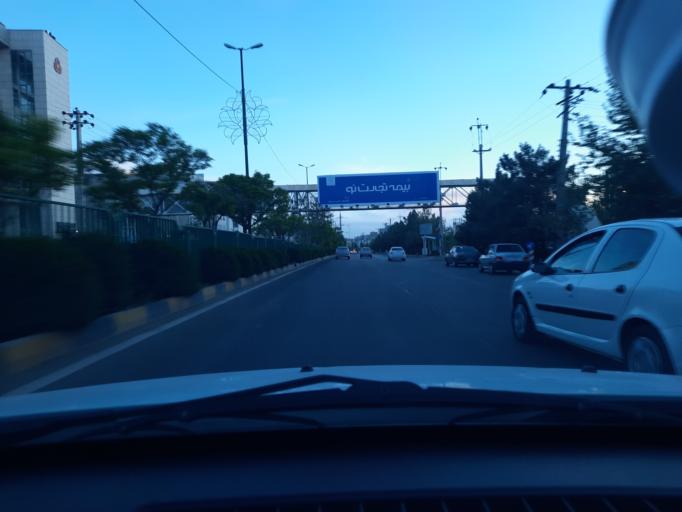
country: IR
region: Qazvin
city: Qazvin
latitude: 36.3086
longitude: 50.0127
